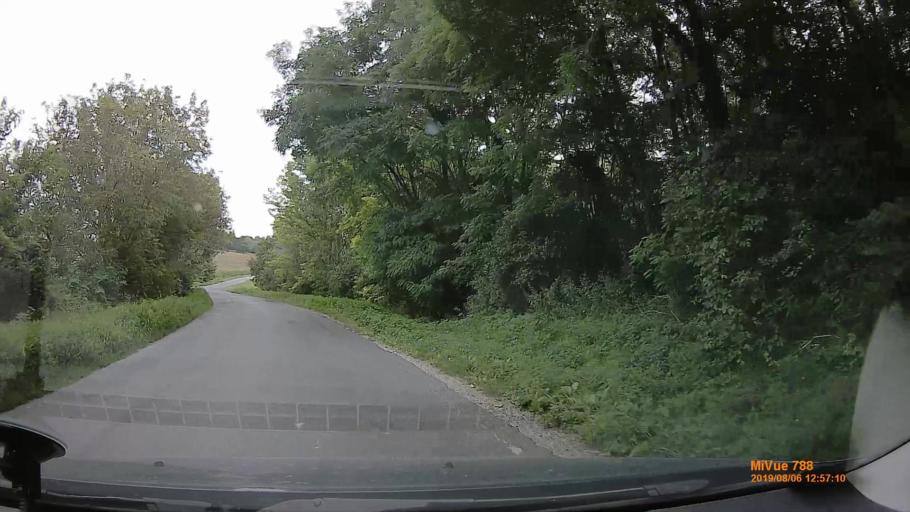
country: HU
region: Zala
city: Pacsa
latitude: 46.6331
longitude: 17.0364
